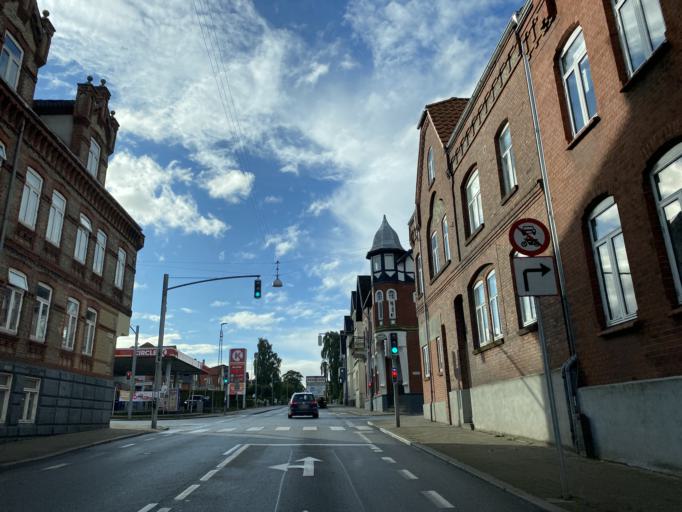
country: DK
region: South Denmark
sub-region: Haderslev Kommune
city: Haderslev
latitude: 55.2456
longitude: 9.4902
